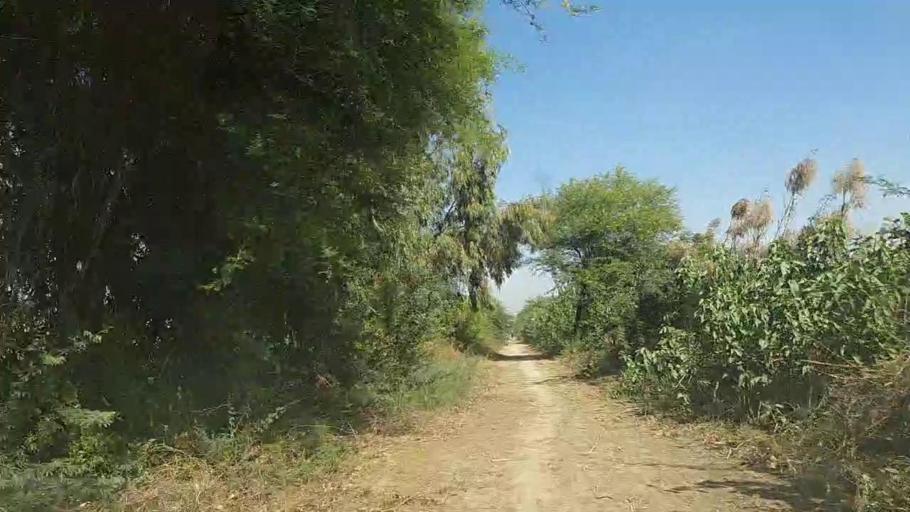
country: PK
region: Sindh
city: Thatta
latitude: 24.8050
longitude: 67.9833
